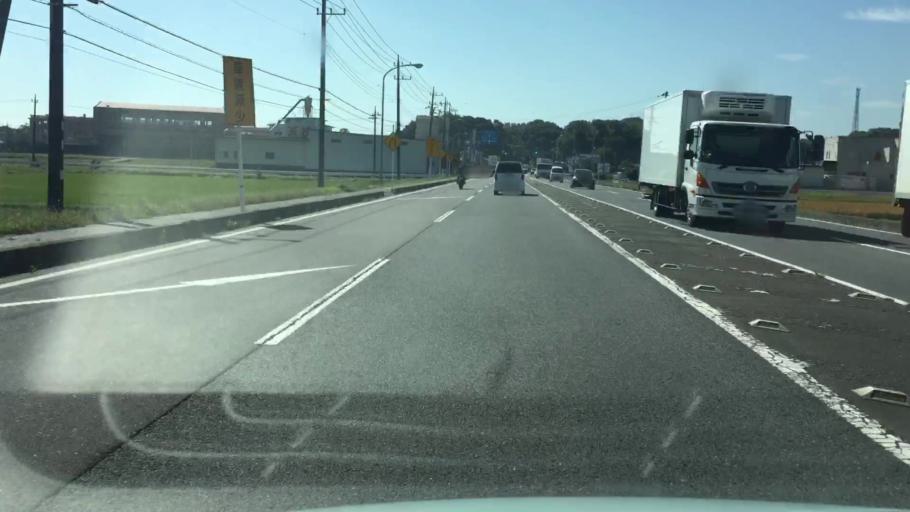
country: JP
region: Ibaraki
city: Ryugasaki
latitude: 35.8853
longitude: 140.1603
